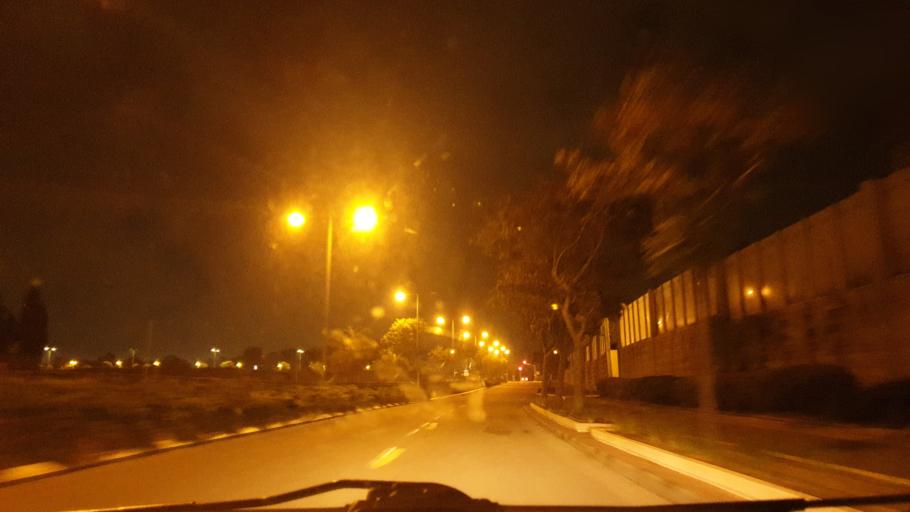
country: IL
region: Central District
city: Bet Dagan
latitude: 31.9700
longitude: 34.8255
